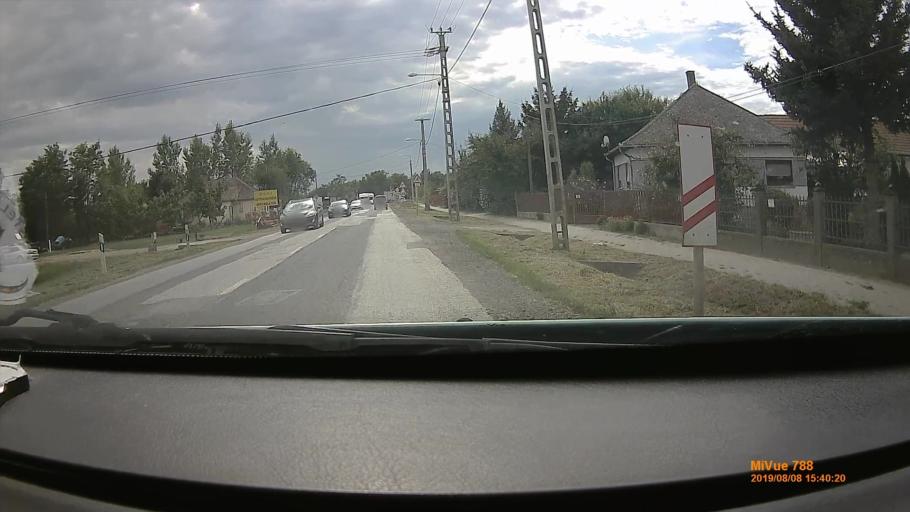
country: HU
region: Szabolcs-Szatmar-Bereg
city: Kocsord
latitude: 47.9375
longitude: 22.4263
